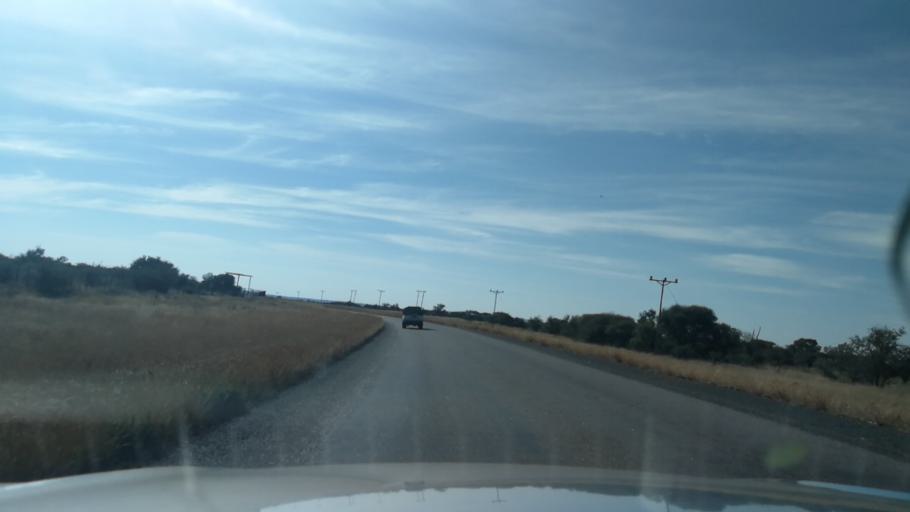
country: BW
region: South East
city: Janeng
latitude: -25.3517
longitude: 25.6274
